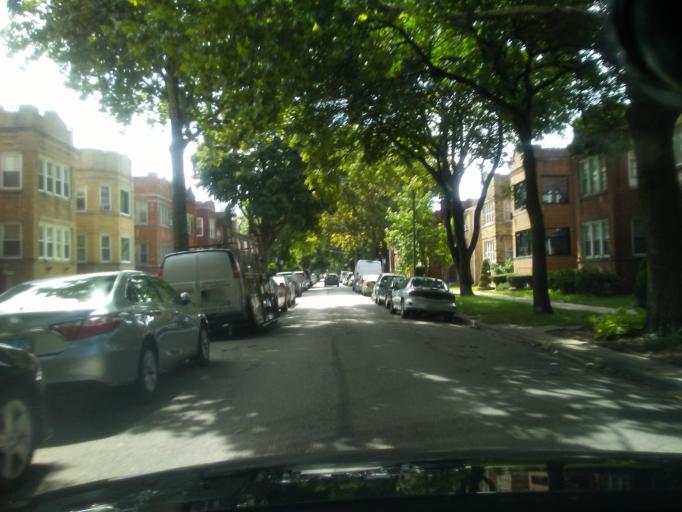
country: US
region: Illinois
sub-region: Cook County
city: Lincolnwood
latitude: 41.9884
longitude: -87.6921
